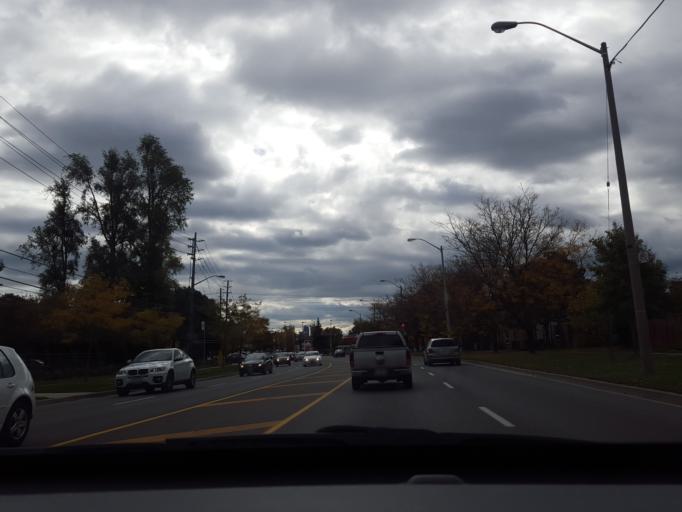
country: CA
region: Ontario
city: Scarborough
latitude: 43.8028
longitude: -79.2978
